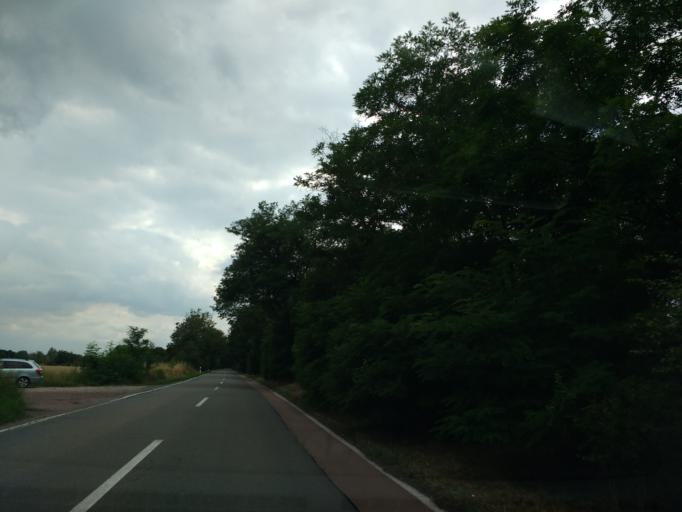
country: DE
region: Saxony-Anhalt
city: Dieskau
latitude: 51.4378
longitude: 12.0247
